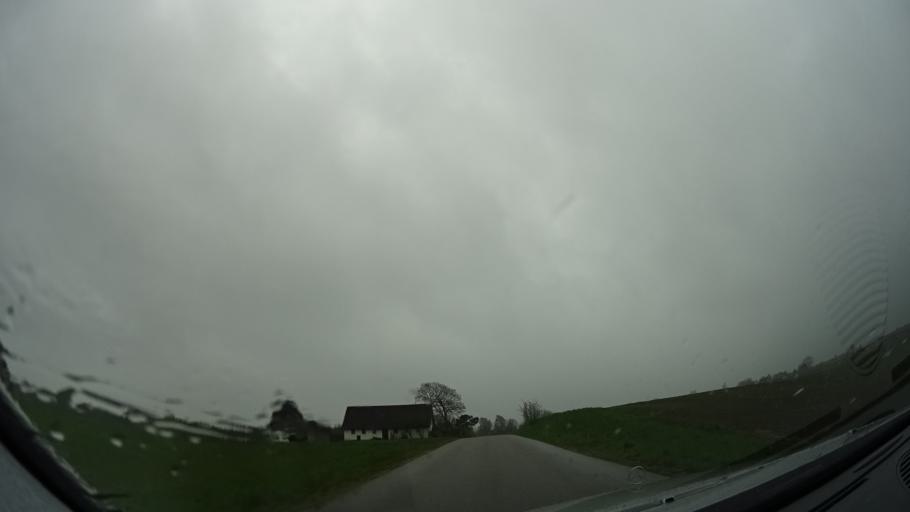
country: DK
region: Zealand
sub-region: Holbaek Kommune
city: Vipperod
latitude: 55.7104
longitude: 11.7729
